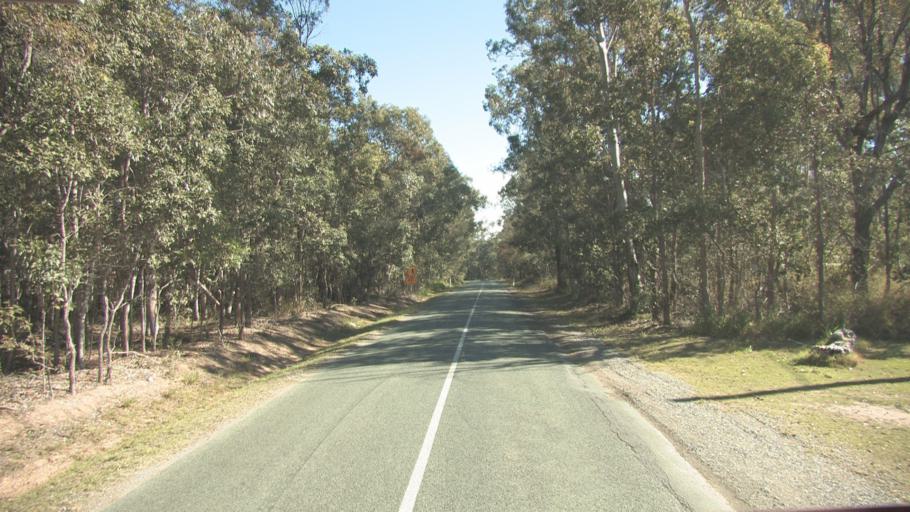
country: AU
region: Queensland
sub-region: Logan
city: Chambers Flat
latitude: -27.7926
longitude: 153.0721
